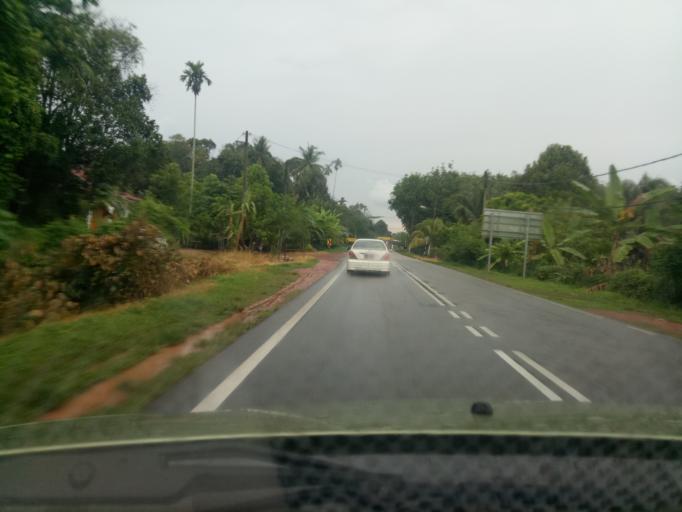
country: MY
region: Penang
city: Tasek Glugor
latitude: 5.5358
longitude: 100.5692
